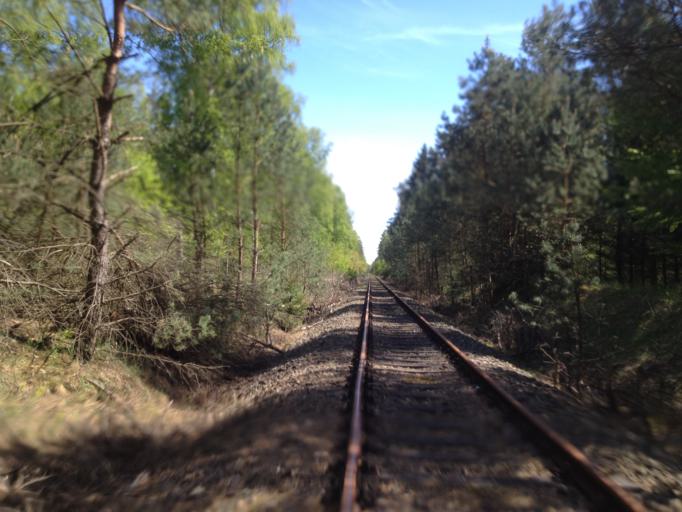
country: DE
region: Brandenburg
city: Lychen
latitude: 53.1669
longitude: 13.3701
